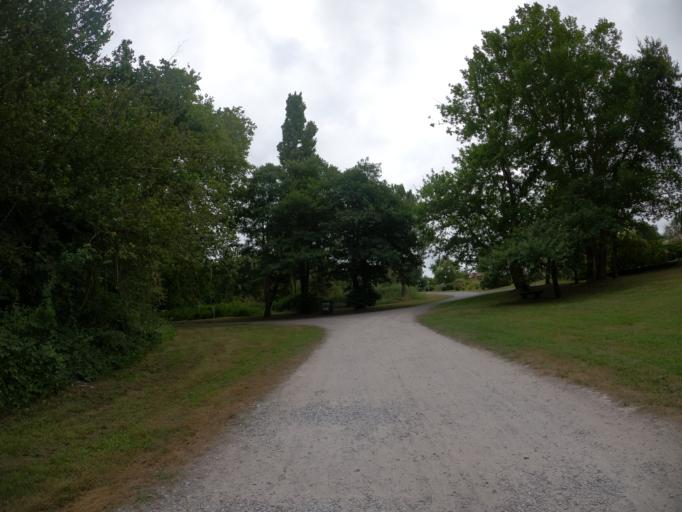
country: FR
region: Aquitaine
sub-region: Departement des Landes
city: Leon
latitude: 43.8852
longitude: -1.3077
